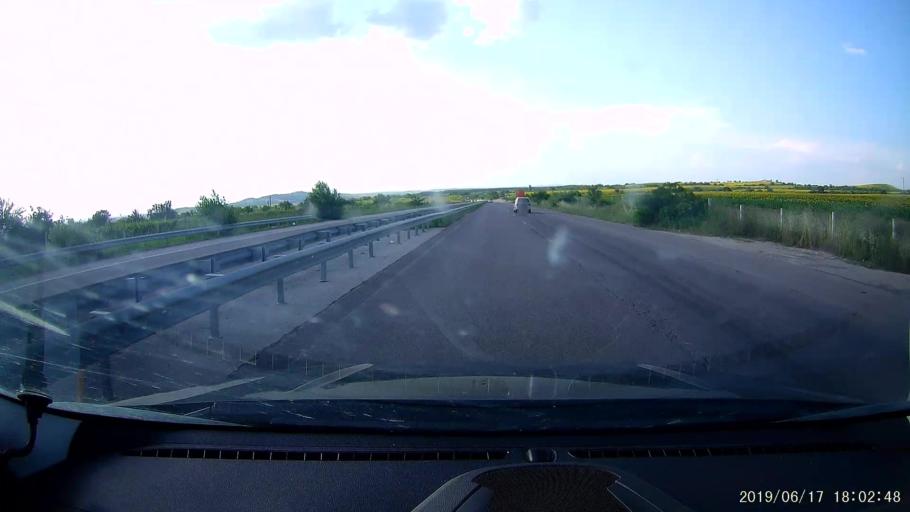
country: BG
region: Khaskovo
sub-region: Obshtina Svilengrad
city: Svilengrad
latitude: 41.7661
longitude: 26.2268
